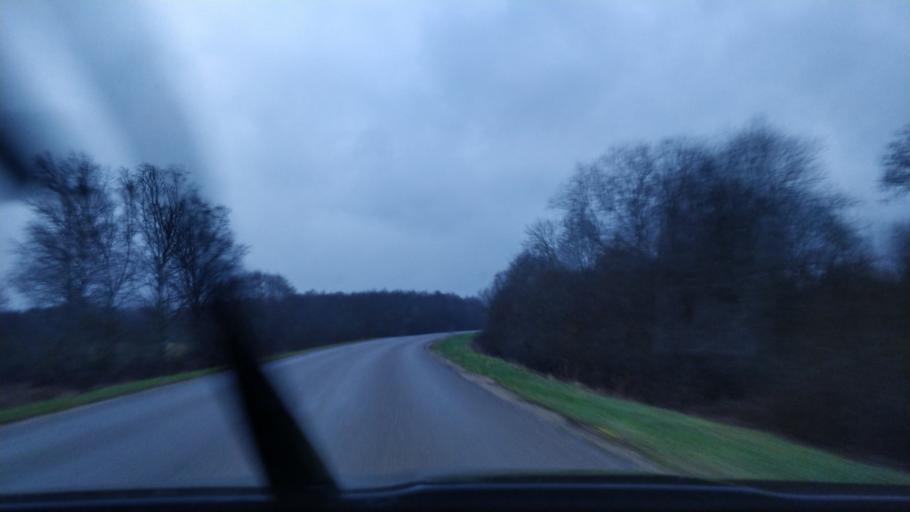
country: EE
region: Laeaene
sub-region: Lihula vald
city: Lihula
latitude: 58.7043
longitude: 23.8616
